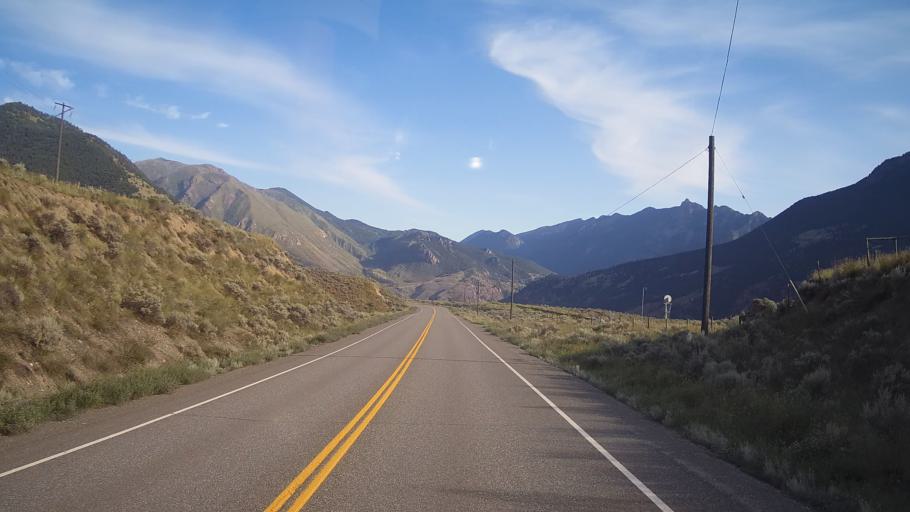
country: CA
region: British Columbia
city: Lillooet
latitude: 50.8052
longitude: -121.8487
